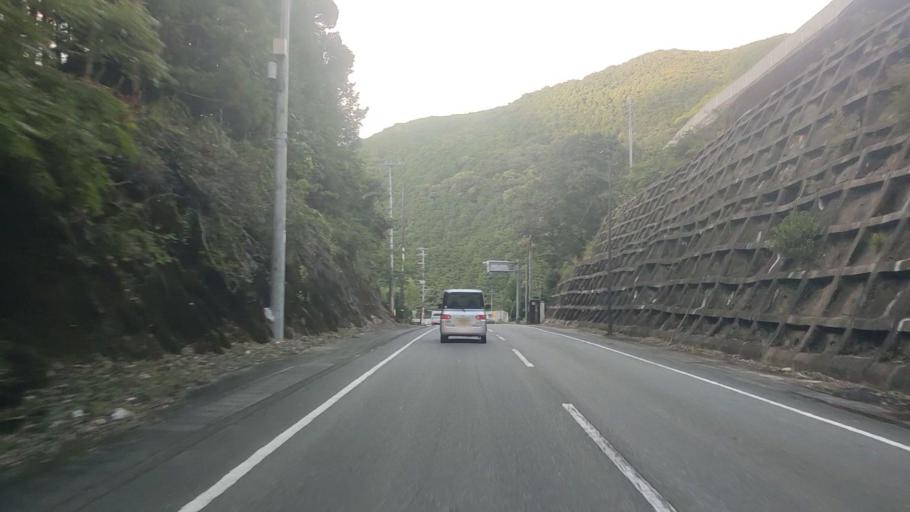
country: JP
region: Wakayama
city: Tanabe
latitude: 33.7813
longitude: 135.5053
